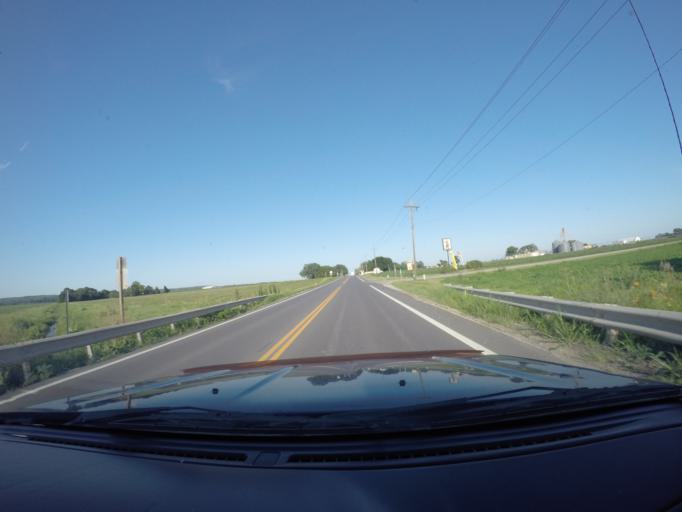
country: US
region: Kansas
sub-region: Douglas County
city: Lawrence
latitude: 39.0006
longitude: -95.2292
